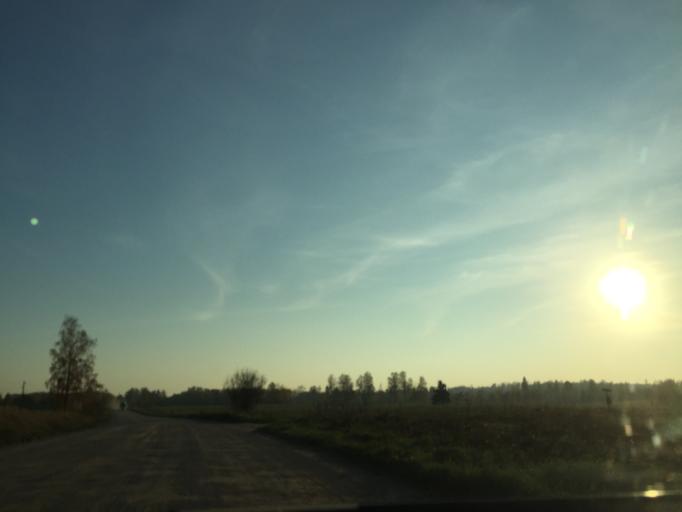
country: LV
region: Vainode
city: Vainode
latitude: 56.5495
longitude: 21.8401
